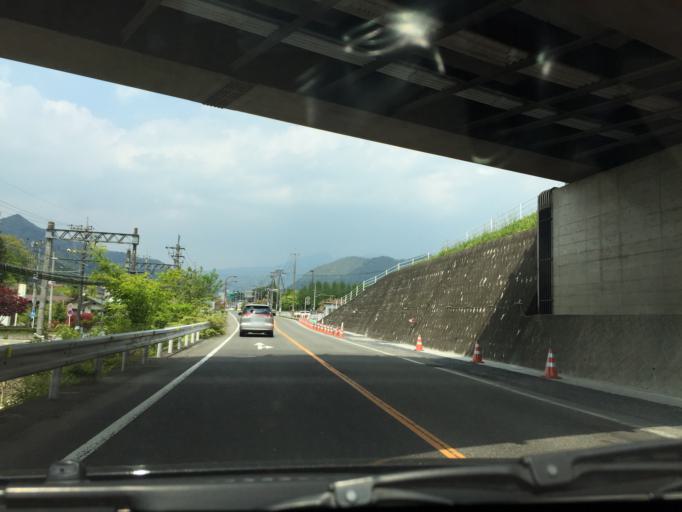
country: JP
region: Tochigi
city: Imaichi
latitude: 36.7979
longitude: 139.7054
